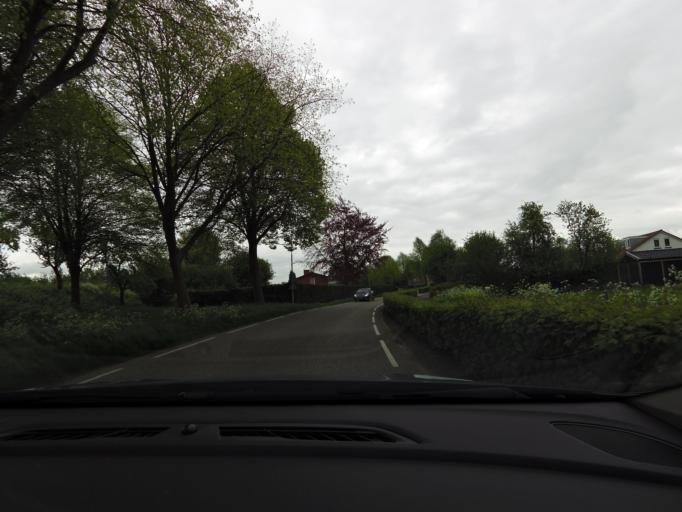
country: NL
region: South Holland
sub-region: Gemeente Leerdam
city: Leerdam
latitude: 51.8870
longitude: 5.0985
